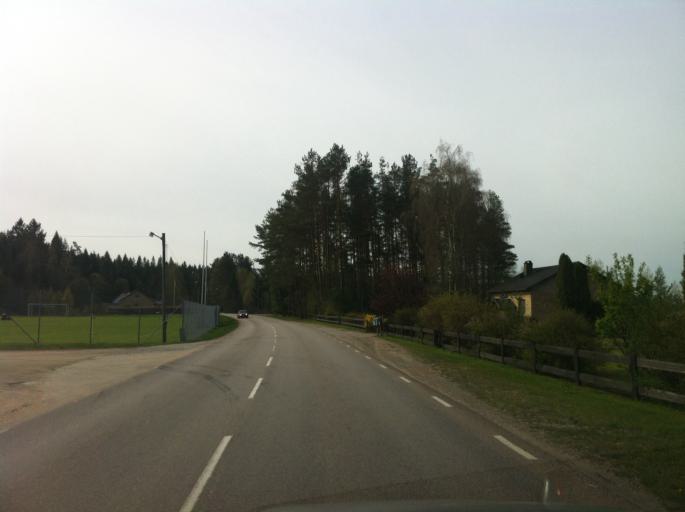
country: SE
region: Vaestra Goetaland
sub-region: Bollebygds Kommun
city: Bollebygd
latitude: 57.7114
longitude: 12.5813
